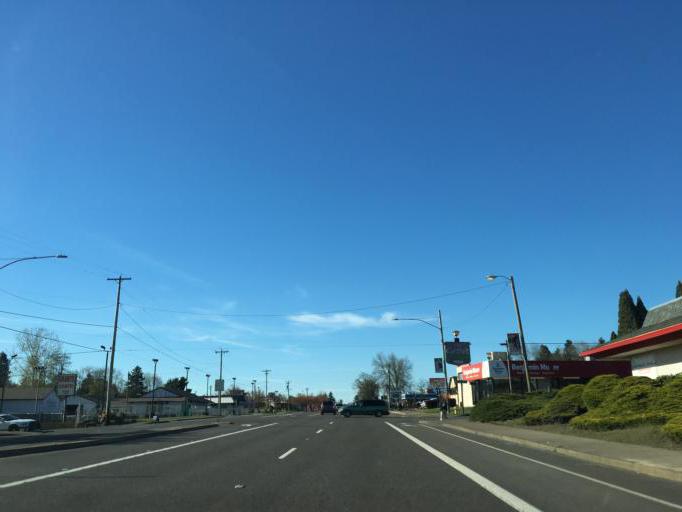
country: US
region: Oregon
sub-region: Clackamas County
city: Oak Grove
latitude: 45.4111
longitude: -122.6281
